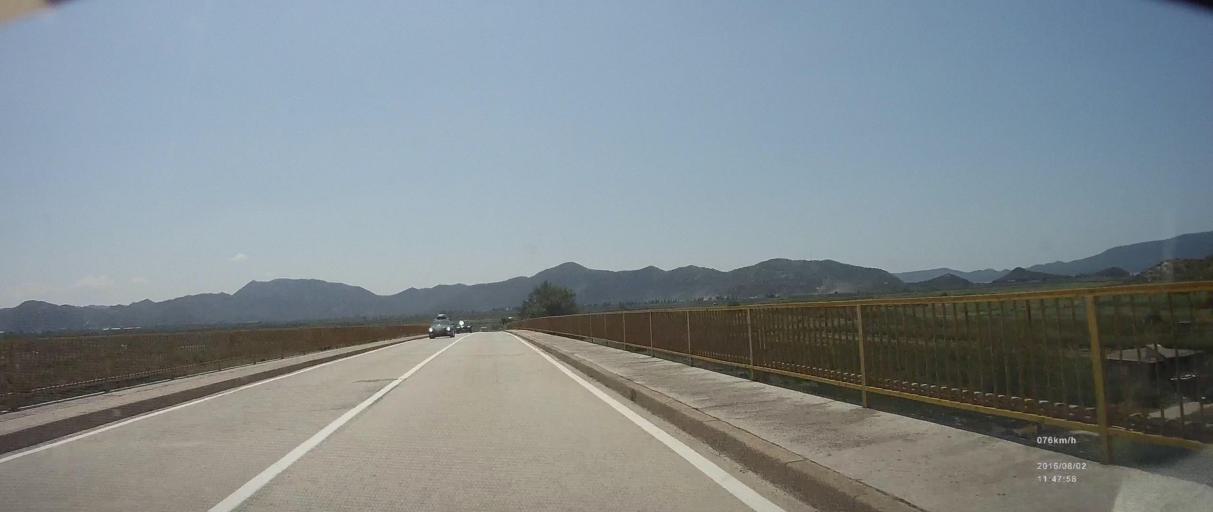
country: HR
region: Dubrovacko-Neretvanska
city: Komin
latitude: 43.0382
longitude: 17.4851
